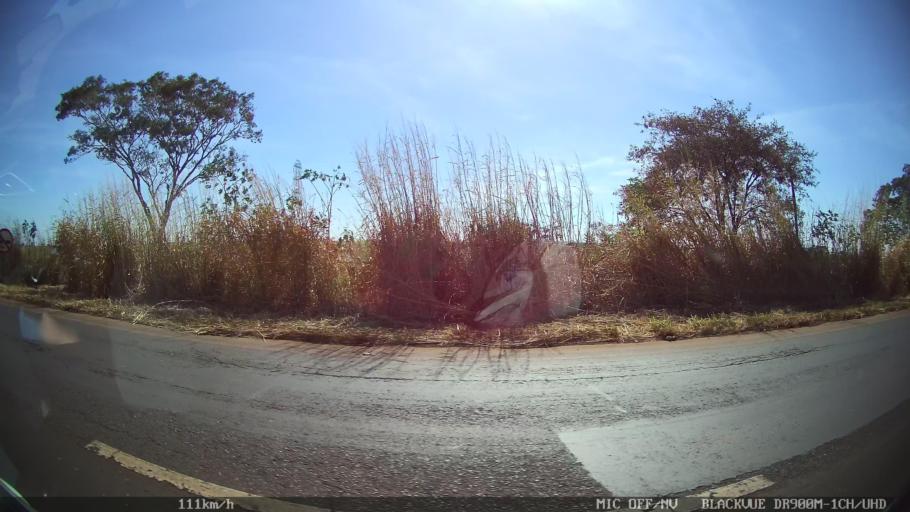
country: BR
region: Sao Paulo
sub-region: Barretos
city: Barretos
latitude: -20.4932
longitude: -48.5270
